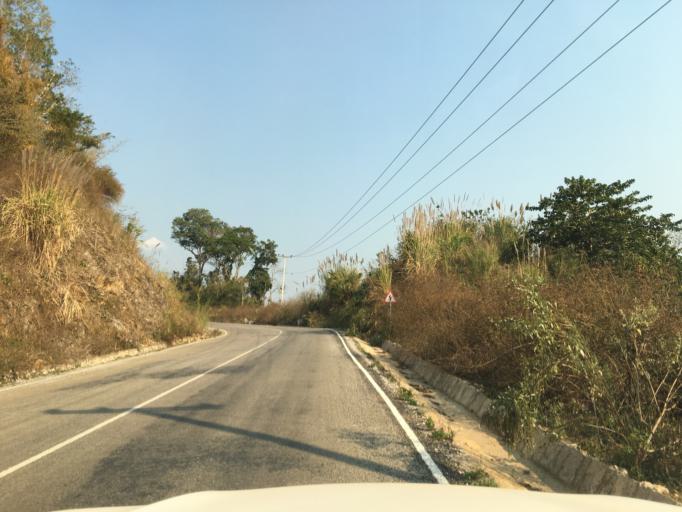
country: LA
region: Houaphan
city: Xam Nua
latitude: 20.5686
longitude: 104.0522
